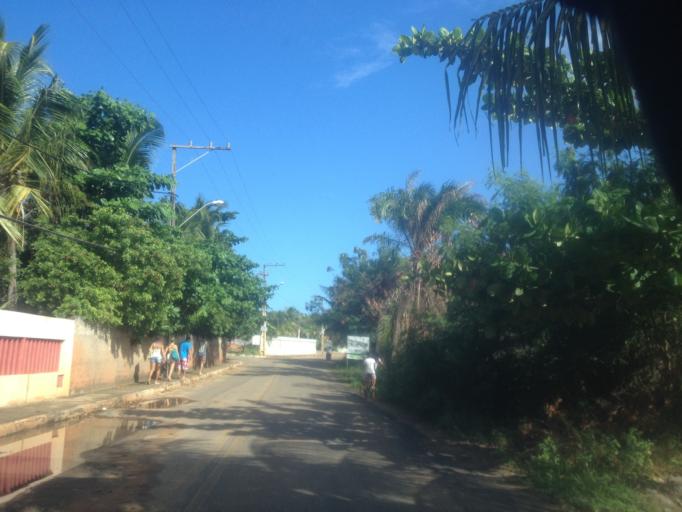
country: BR
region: Bahia
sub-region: Mata De Sao Joao
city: Mata de Sao Joao
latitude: -12.6259
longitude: -38.0484
